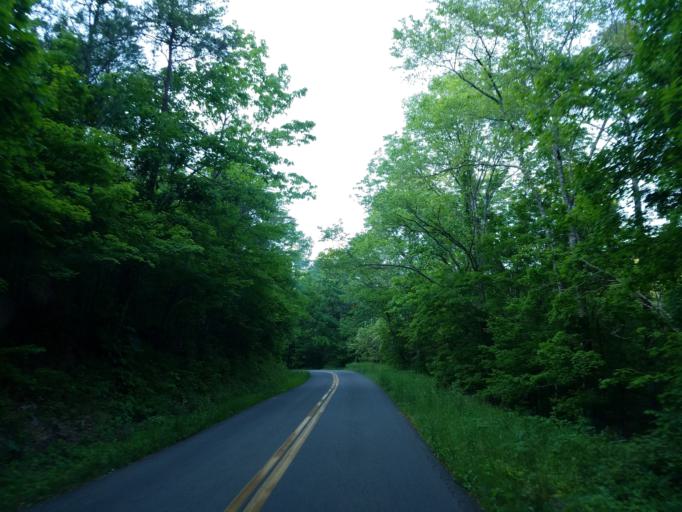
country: US
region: Georgia
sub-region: Gordon County
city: Calhoun
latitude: 34.5679
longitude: -85.1005
